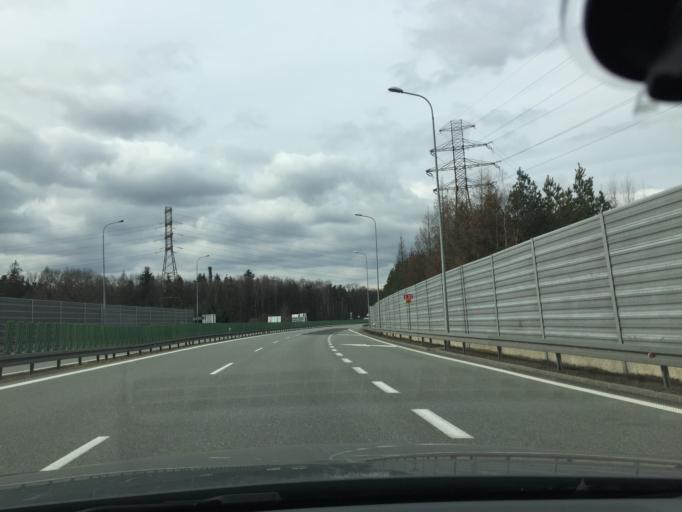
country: PL
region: Silesian Voivodeship
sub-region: Powiat cieszynski
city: Skoczow
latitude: 49.7849
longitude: 18.7968
